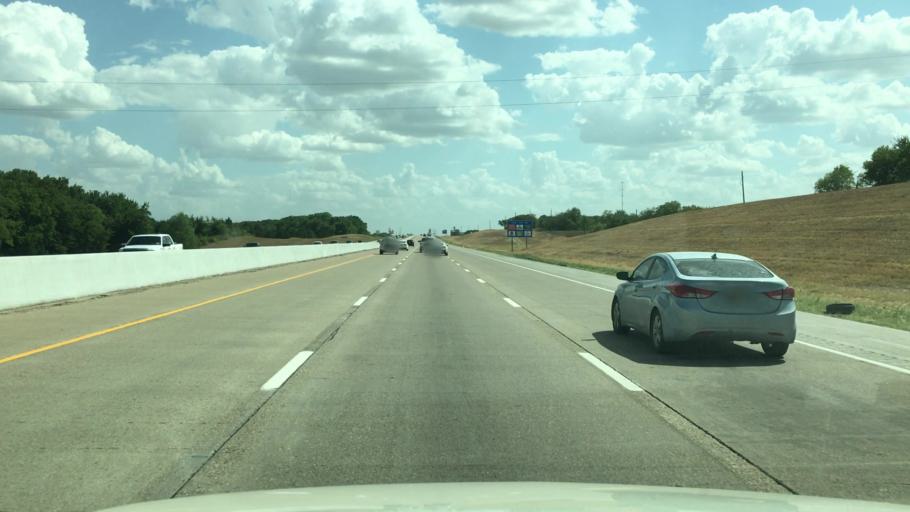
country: US
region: Texas
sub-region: Ellis County
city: Italy
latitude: 32.2134
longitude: -96.8909
